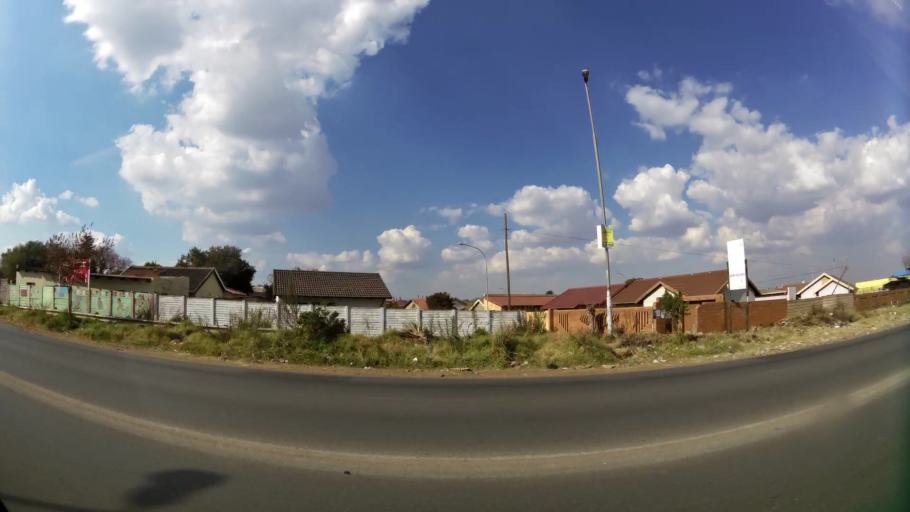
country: ZA
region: Gauteng
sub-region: City of Johannesburg Metropolitan Municipality
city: Roodepoort
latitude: -26.2107
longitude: 27.8702
